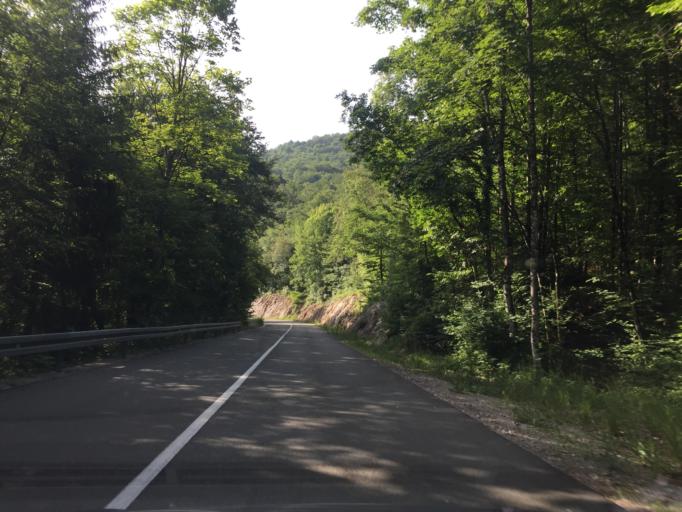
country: HR
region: Primorsko-Goranska
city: Matulji
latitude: 45.4074
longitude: 14.2546
